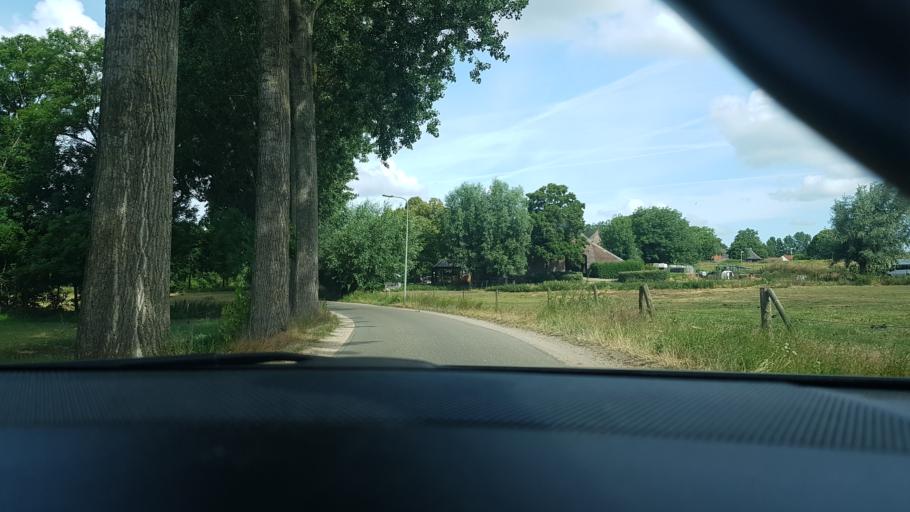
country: NL
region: Limburg
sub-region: Gemeente Roermond
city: Leeuwen
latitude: 51.2230
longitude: 6.0143
